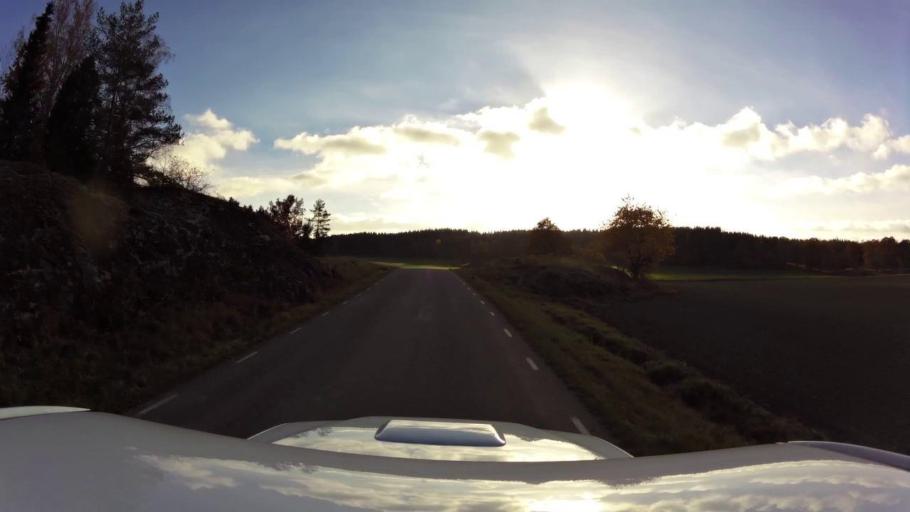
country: SE
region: OEstergoetland
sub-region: Linkopings Kommun
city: Vikingstad
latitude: 58.2803
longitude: 15.4351
